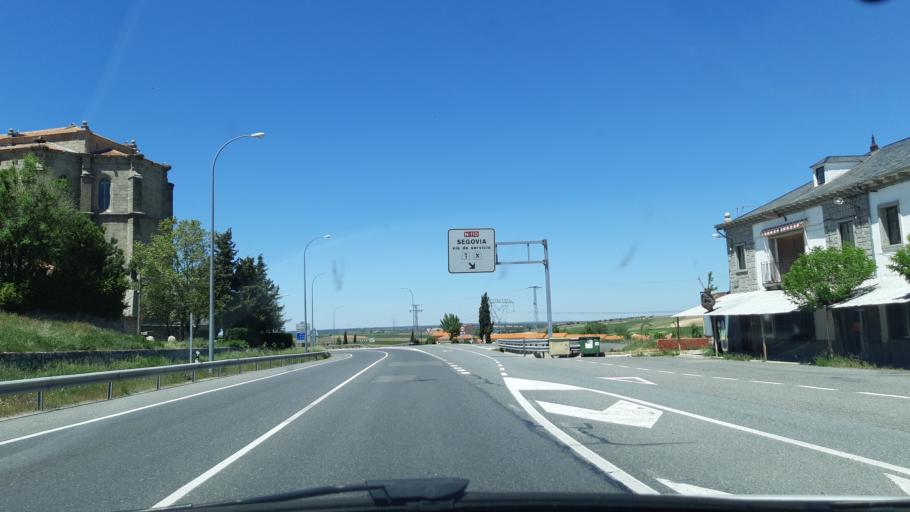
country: ES
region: Castille and Leon
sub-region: Provincia de Segovia
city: Villacastin
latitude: 40.7809
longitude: -4.4105
